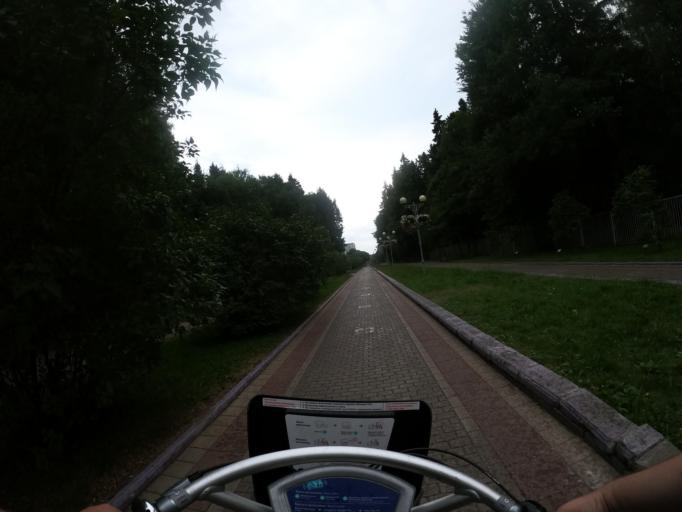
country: RU
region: Moskovskaya
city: Troitsk
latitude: 55.4742
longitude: 37.2956
